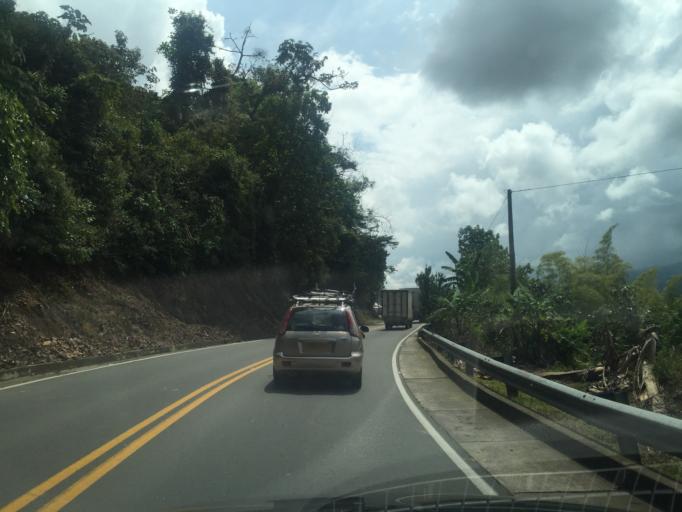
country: CO
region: Caldas
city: Villamaria
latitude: 5.0110
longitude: -75.5510
